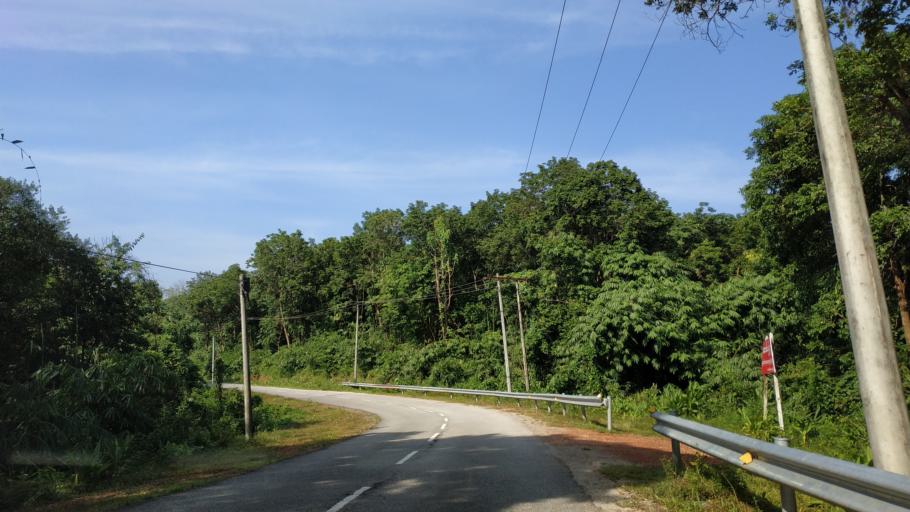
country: TH
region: Kanchanaburi
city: Thong Pha Phum
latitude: 14.6101
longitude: 98.1091
